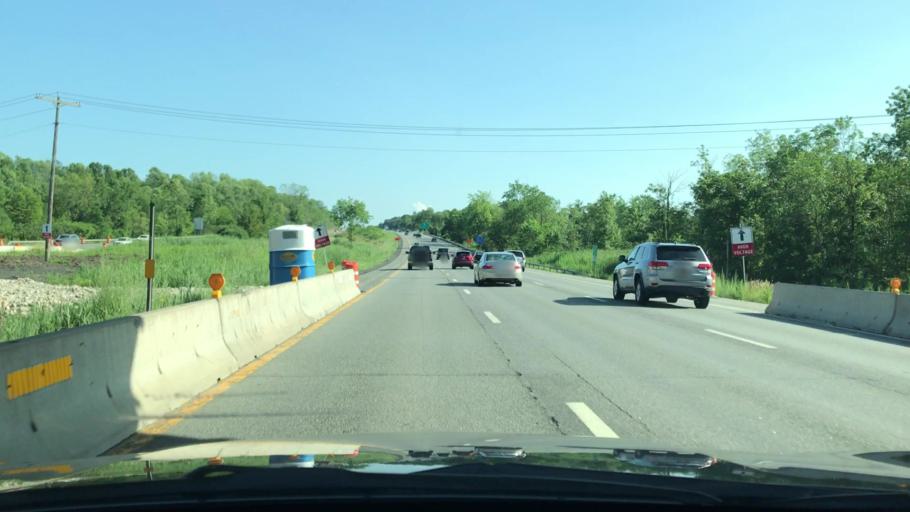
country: US
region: New York
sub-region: Saratoga County
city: Ballston Spa
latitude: 42.9957
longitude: -73.8039
